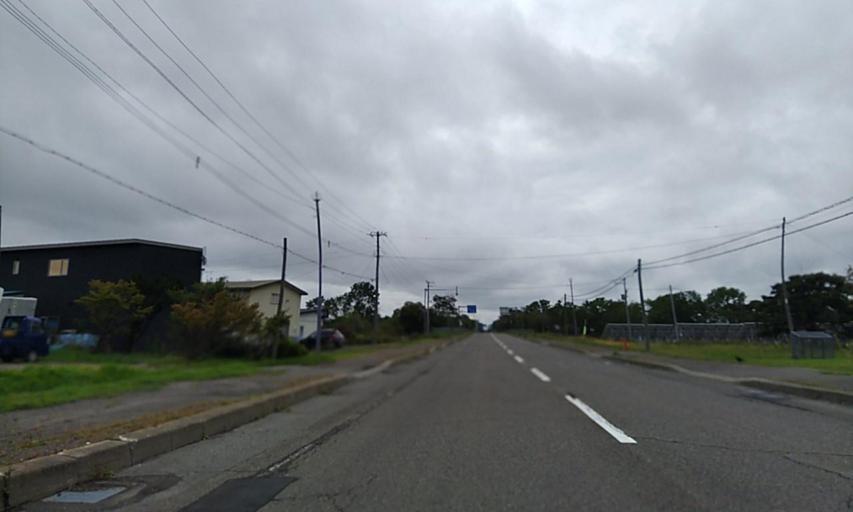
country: JP
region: Hokkaido
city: Nemuro
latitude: 43.3832
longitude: 145.2861
